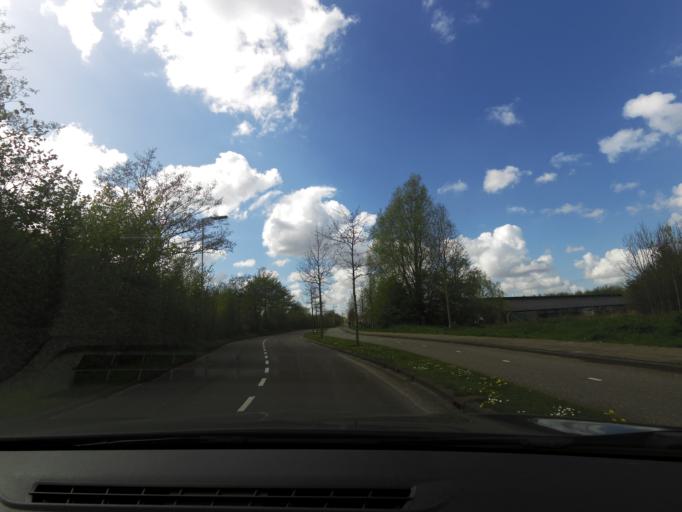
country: NL
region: South Holland
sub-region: Gemeente Albrandswaard
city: Rhoon
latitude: 51.8599
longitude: 4.4077
